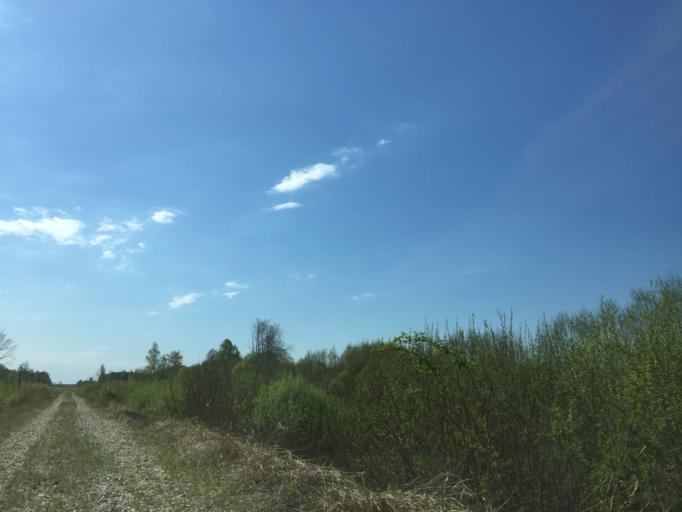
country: LV
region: Saulkrastu
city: Saulkrasti
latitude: 57.3506
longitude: 24.4910
